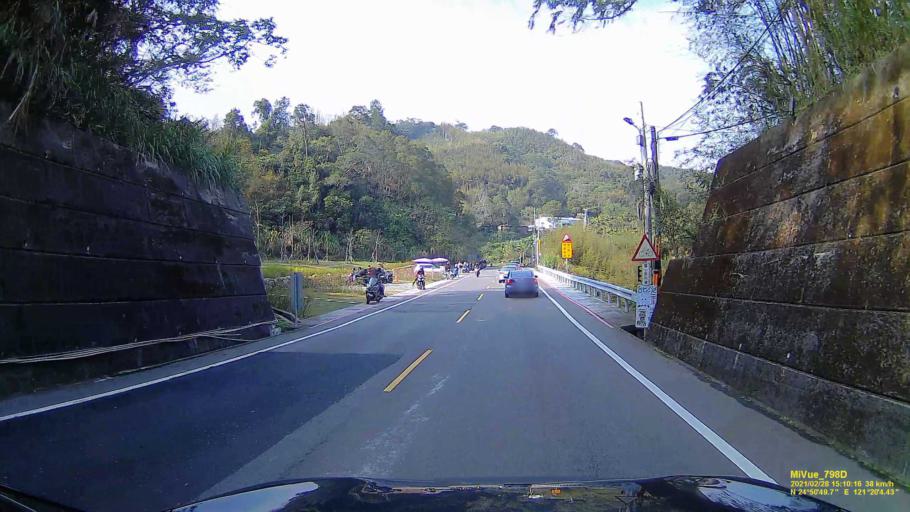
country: TW
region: Taiwan
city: Daxi
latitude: 24.8474
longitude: 121.3345
